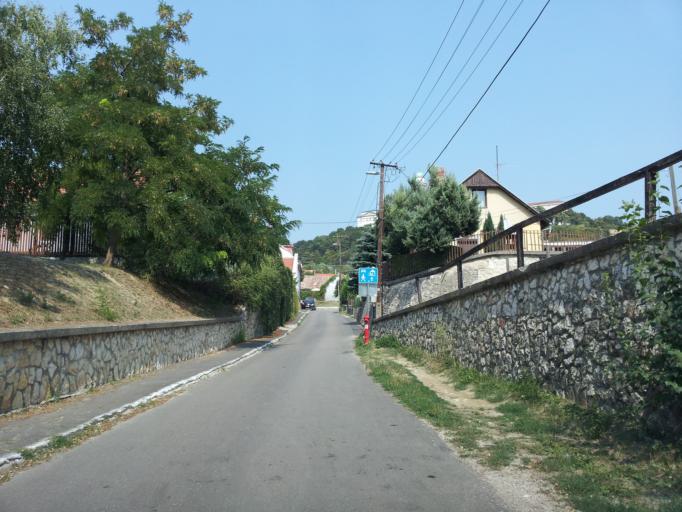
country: HU
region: Gyor-Moson-Sopron
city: Pannonhalma
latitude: 47.5507
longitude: 17.7551
